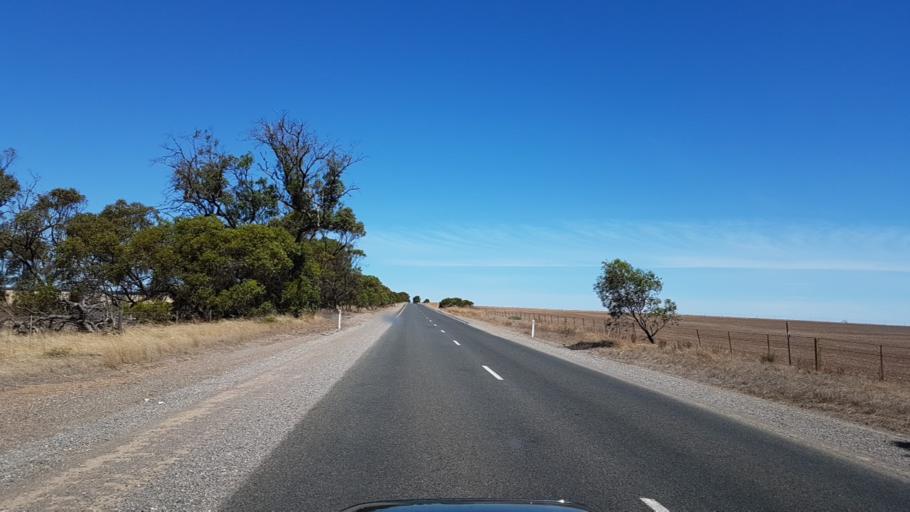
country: AU
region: South Australia
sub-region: Yorke Peninsula
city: Maitland
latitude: -34.3406
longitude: 137.6579
